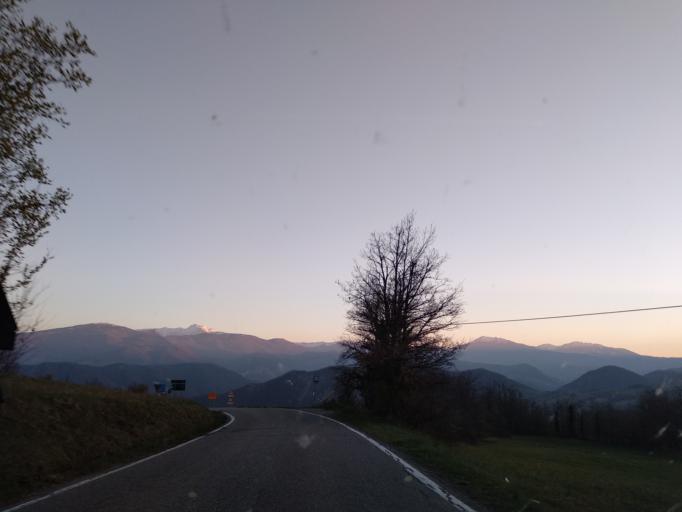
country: IT
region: Emilia-Romagna
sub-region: Provincia di Reggio Emilia
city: Castelnovo ne'Monti
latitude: 44.4128
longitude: 10.4024
